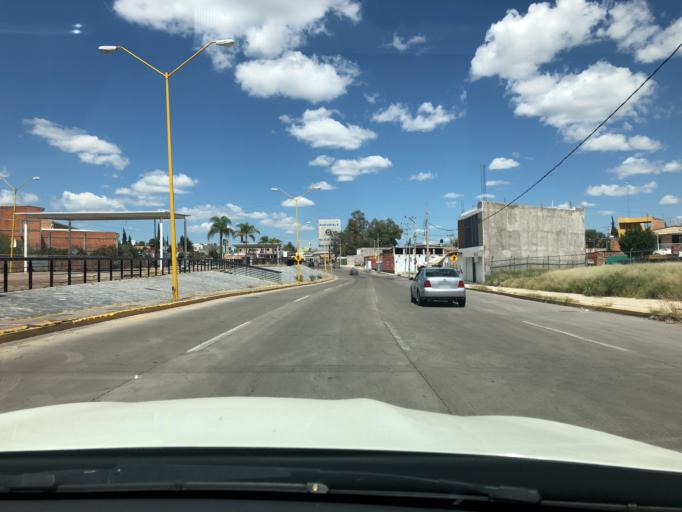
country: MX
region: Aguascalientes
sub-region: Aguascalientes
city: La Loma de los Negritos
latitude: 21.8700
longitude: -102.3155
